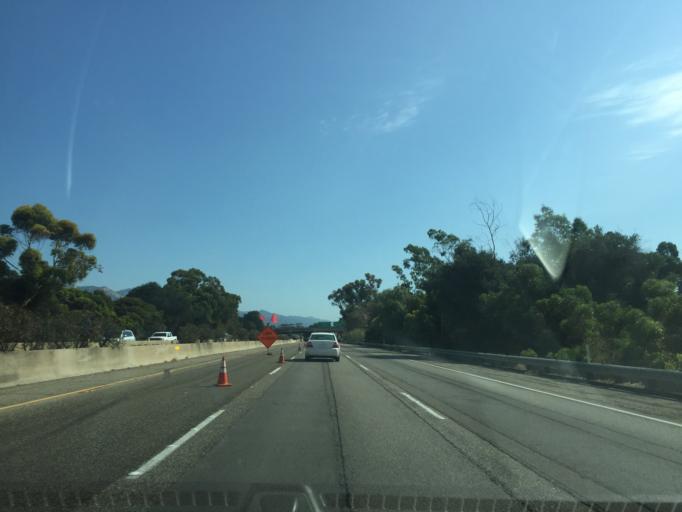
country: US
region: California
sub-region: Santa Barbara County
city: Goleta
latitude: 34.4407
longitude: -119.8187
